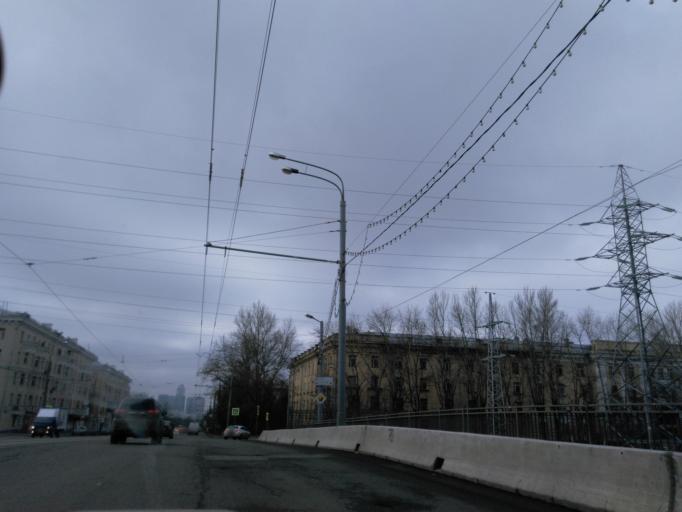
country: RU
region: Moscow
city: Pokrovskoye-Streshnevo
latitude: 55.8355
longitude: 37.4540
